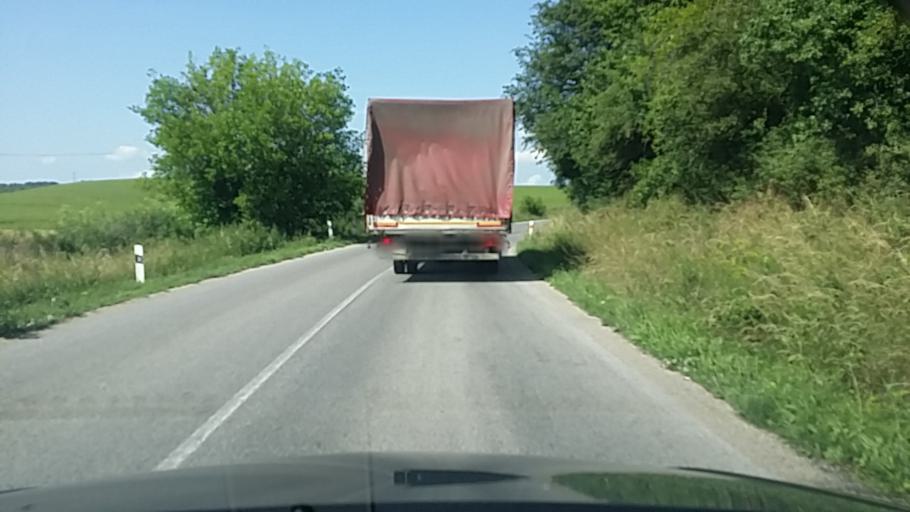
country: SK
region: Nitriansky
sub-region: Okres Nove Zamky
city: Sturovo
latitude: 47.8396
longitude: 18.7229
